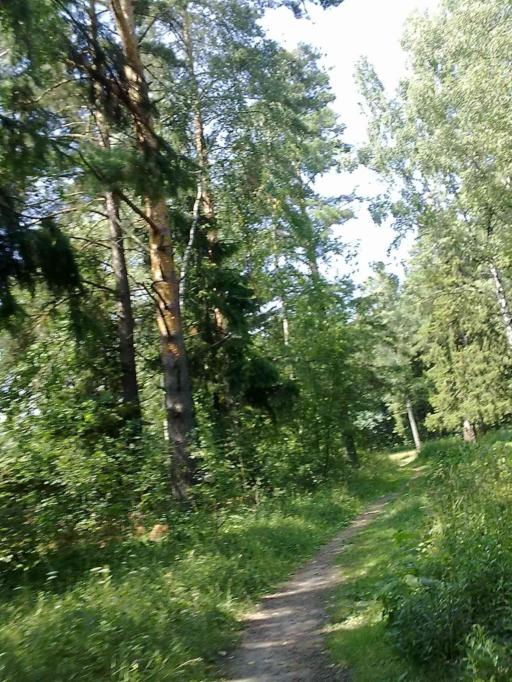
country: RU
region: Moscow
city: Tolstopal'tsevo
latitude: 55.6147
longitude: 37.2261
